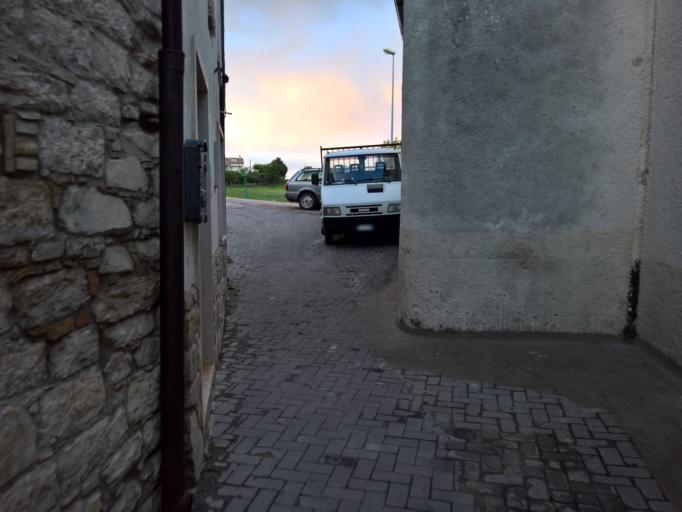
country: IT
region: Apulia
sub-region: Provincia di Foggia
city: Castelluccio Valmaggiore
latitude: 41.3426
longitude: 15.1986
